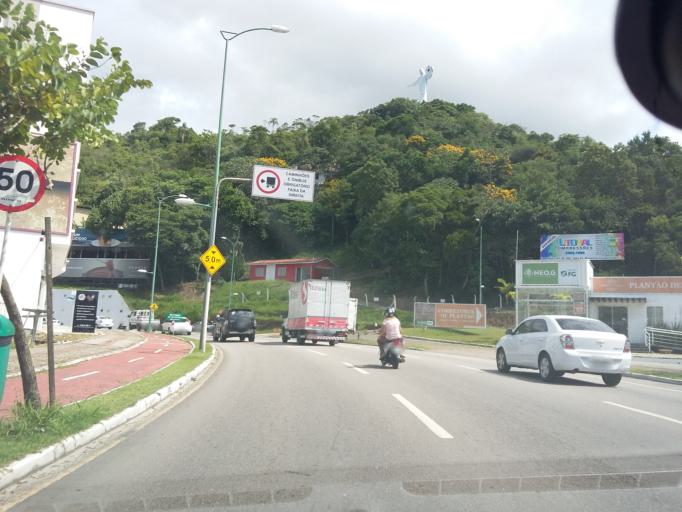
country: BR
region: Santa Catarina
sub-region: Balneario Camboriu
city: Balneario Camboriu
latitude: -26.9829
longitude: -48.6432
